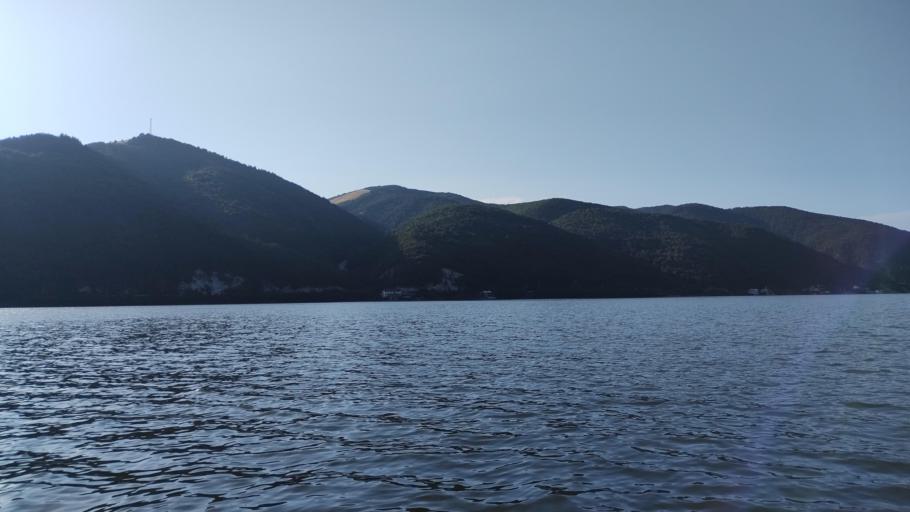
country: RO
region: Mehedinti
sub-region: Comuna Dubova
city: Dubova
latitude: 44.5529
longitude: 22.2286
